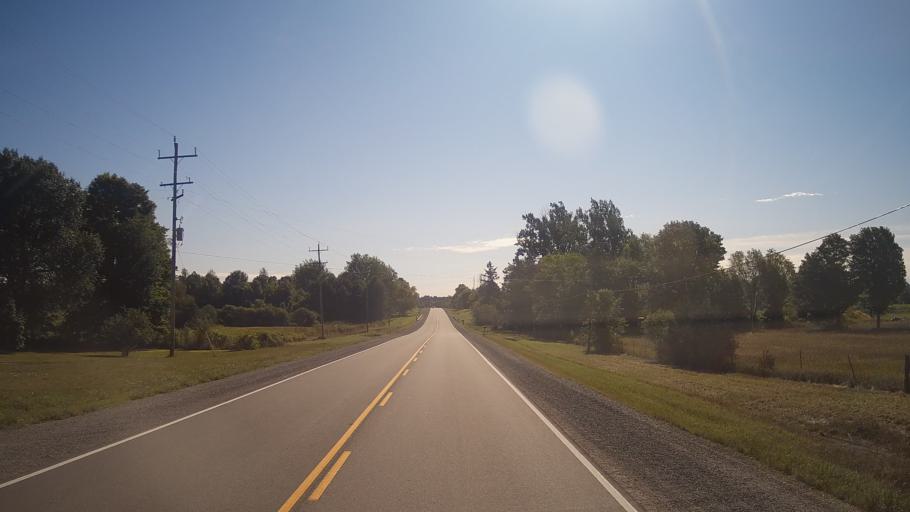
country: CA
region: Ontario
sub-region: Lanark County
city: Smiths Falls
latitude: 44.6267
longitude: -76.0079
